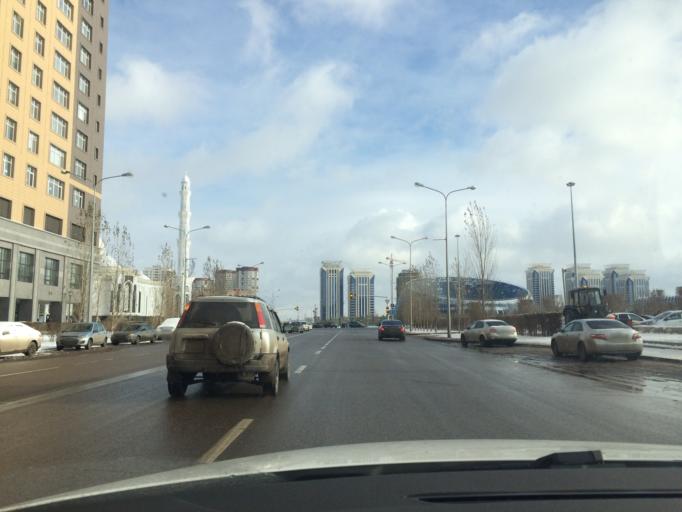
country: KZ
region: Astana Qalasy
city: Astana
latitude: 51.1252
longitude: 71.4672
